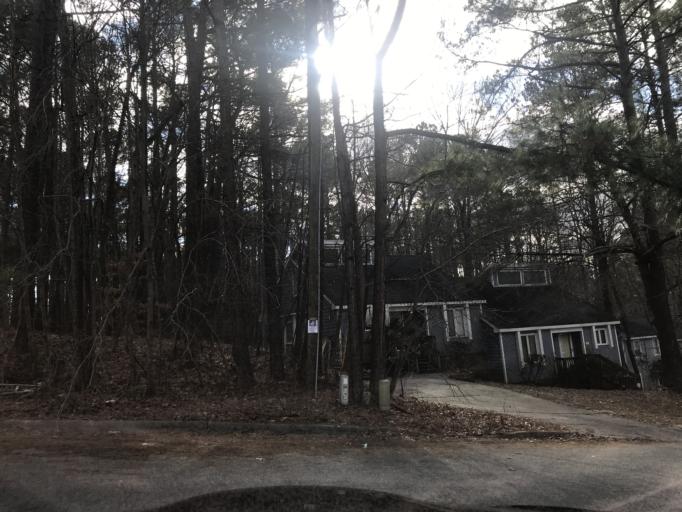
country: US
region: North Carolina
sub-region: Wake County
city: West Raleigh
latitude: 35.7714
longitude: -78.7180
